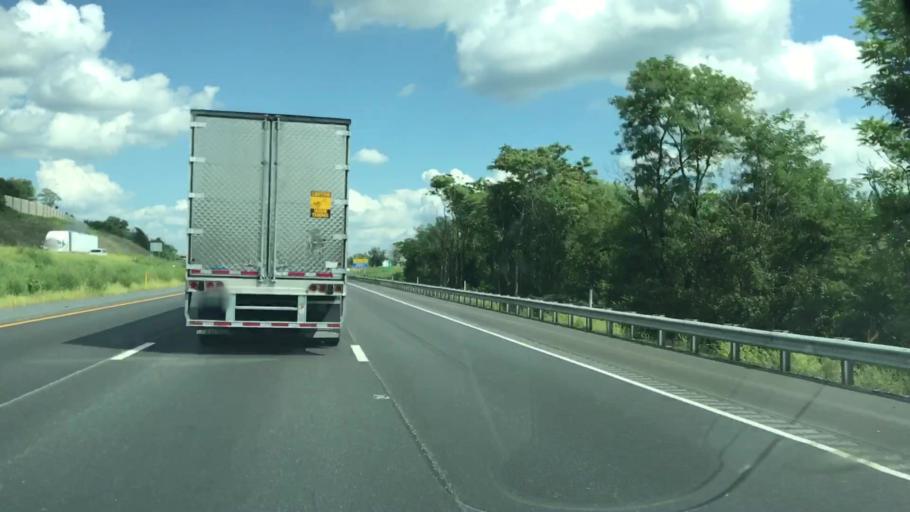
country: US
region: Pennsylvania
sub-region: Cumberland County
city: Mechanicsburg
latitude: 40.2713
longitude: -77.0321
